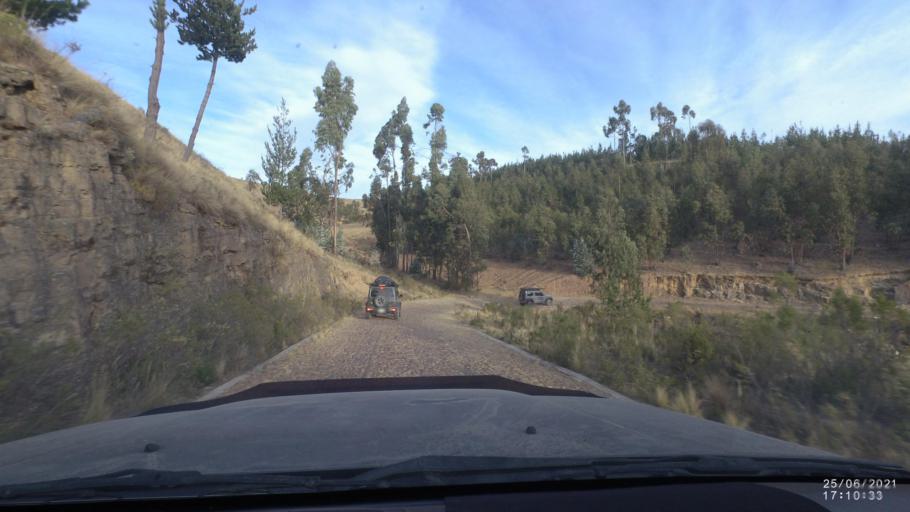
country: BO
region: Cochabamba
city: Arani
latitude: -17.8424
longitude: -65.7027
